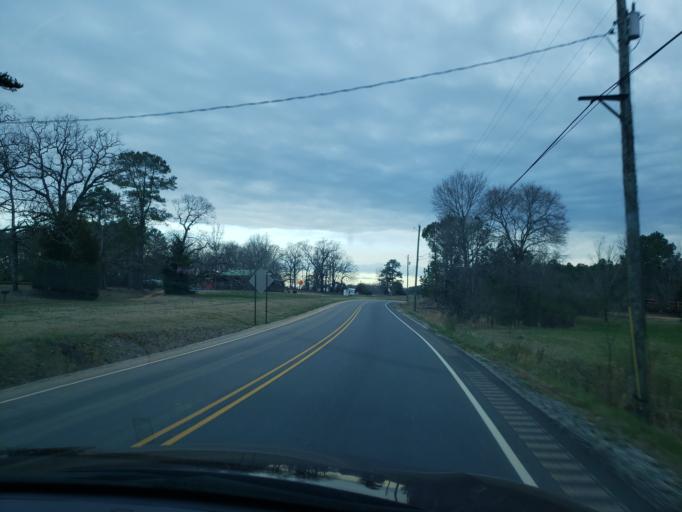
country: US
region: Alabama
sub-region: Randolph County
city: Roanoke
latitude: 33.0565
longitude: -85.3312
